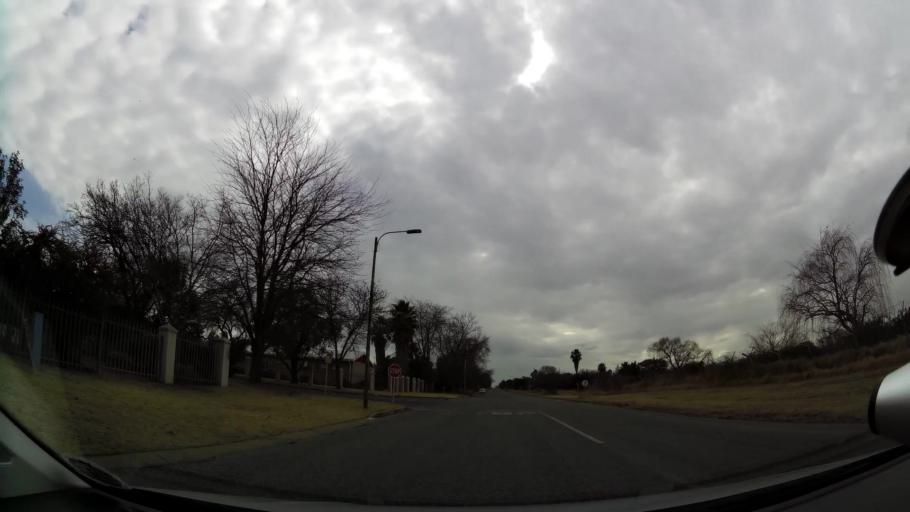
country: ZA
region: Orange Free State
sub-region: Fezile Dabi District Municipality
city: Kroonstad
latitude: -27.6405
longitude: 27.2386
